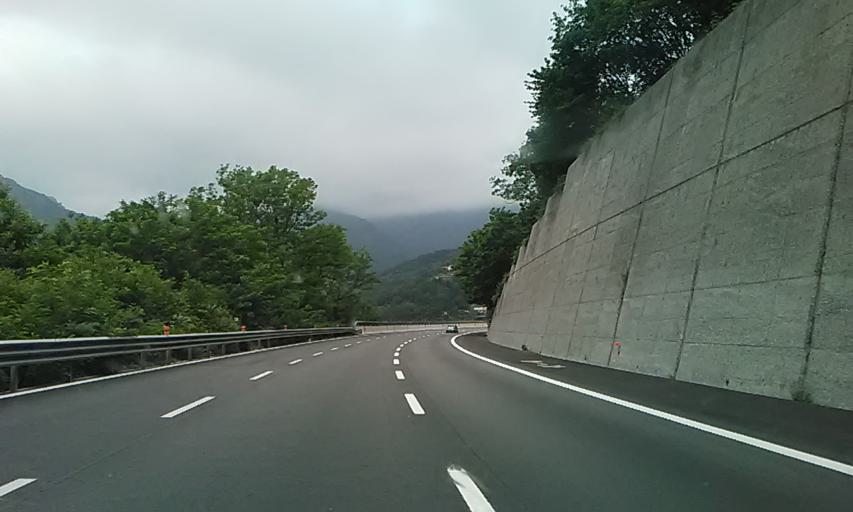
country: IT
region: Liguria
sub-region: Provincia di Genova
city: Mele
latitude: 44.4476
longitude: 8.7327
